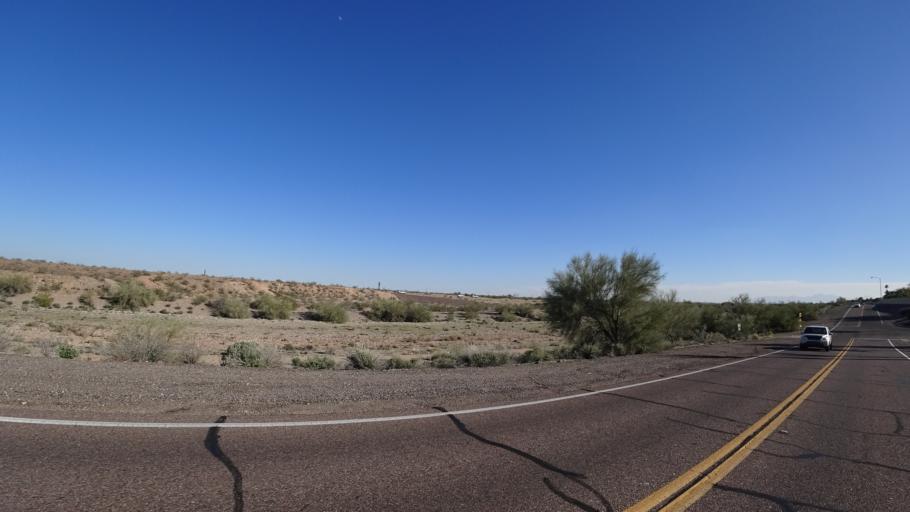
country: US
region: Arizona
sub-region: Maricopa County
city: Sun City West
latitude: 33.6684
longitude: -112.3256
